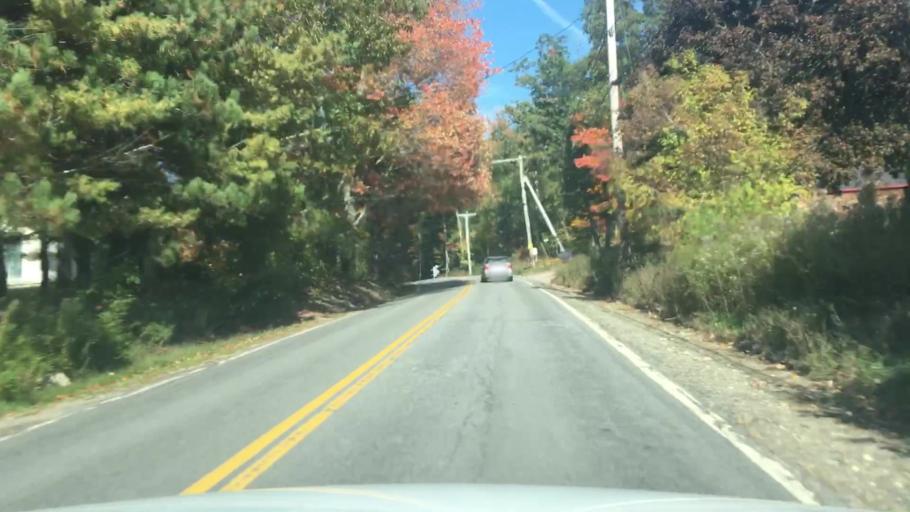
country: US
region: Maine
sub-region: Knox County
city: Warren
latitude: 44.1405
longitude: -69.2356
